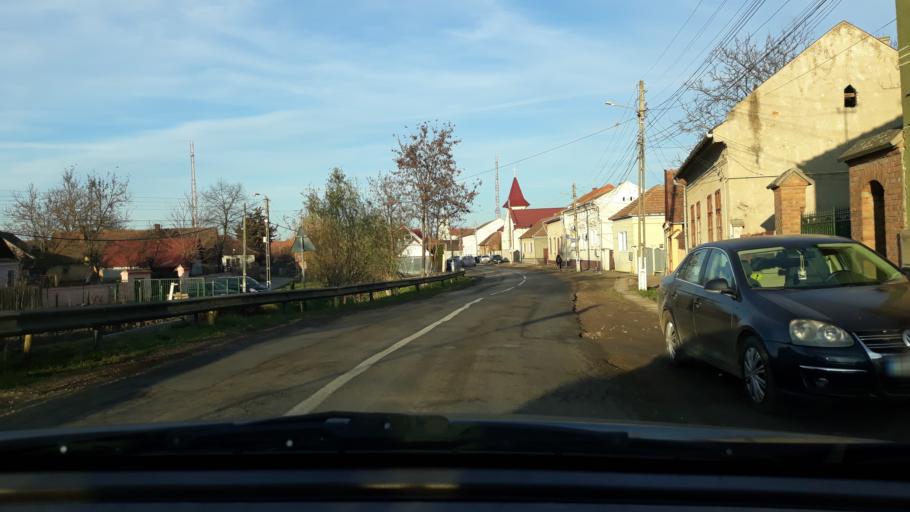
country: RO
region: Bihor
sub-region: Comuna Suplacu de Barcau
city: Suplacu de Barcau
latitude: 47.2543
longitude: 22.5308
